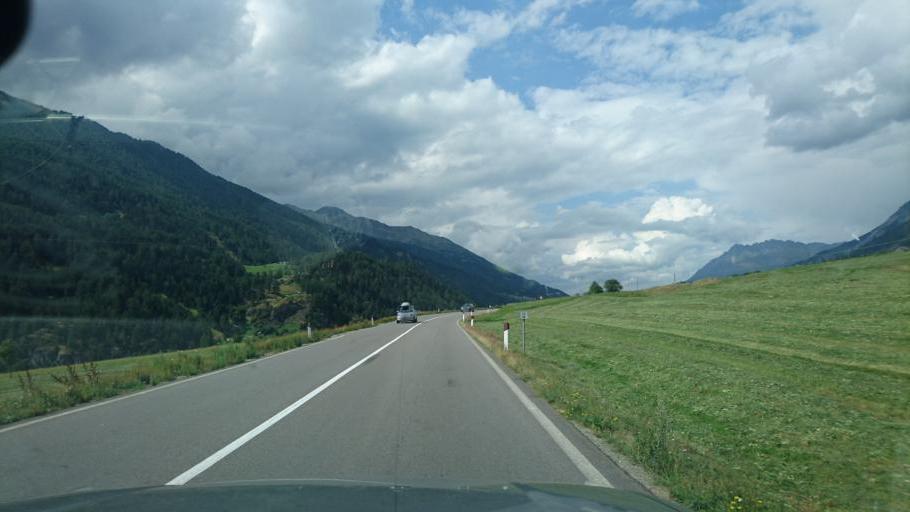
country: IT
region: Trentino-Alto Adige
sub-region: Bolzano
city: Malles Venosta
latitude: 46.7277
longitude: 10.5392
